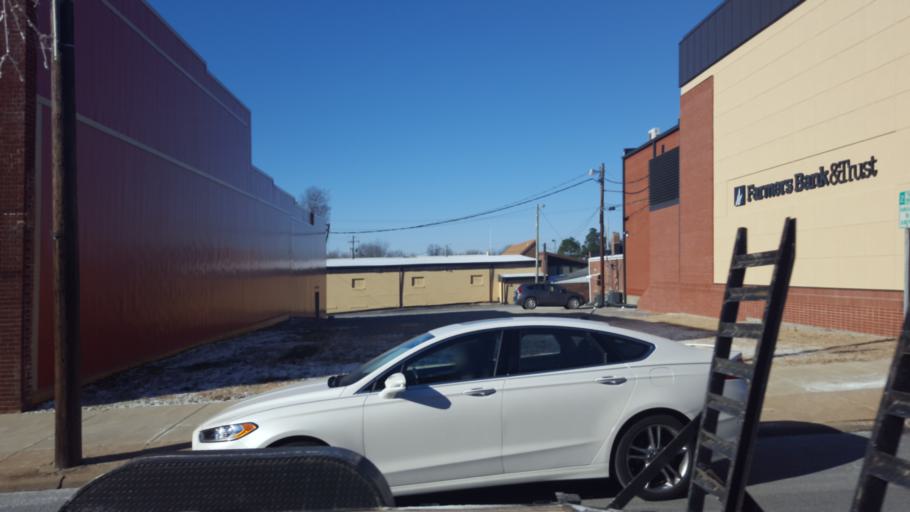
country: US
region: Kentucky
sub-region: Crittenden County
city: Marion
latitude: 37.3319
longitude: -88.0815
